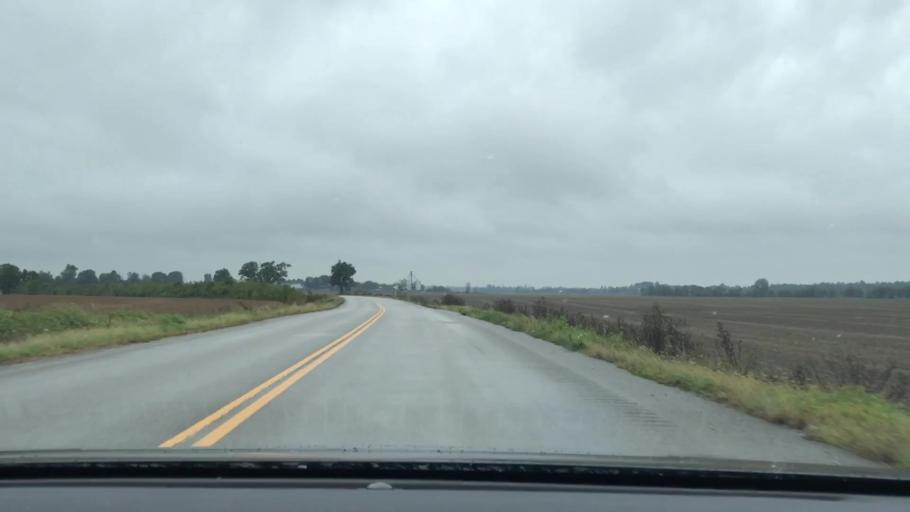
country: US
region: Kentucky
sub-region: Hopkins County
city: Madisonville
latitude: 37.3821
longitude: -87.3399
